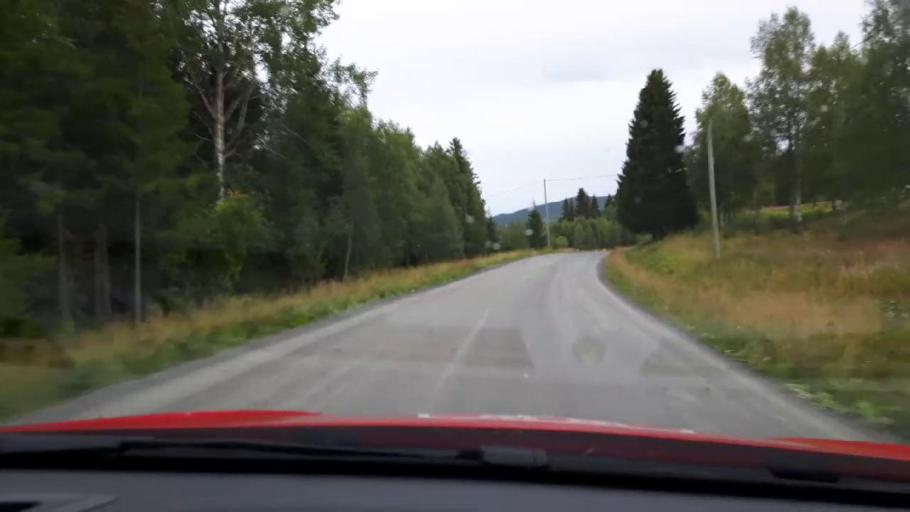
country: SE
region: Jaemtland
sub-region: Are Kommun
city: Jarpen
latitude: 63.4187
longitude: 13.3519
